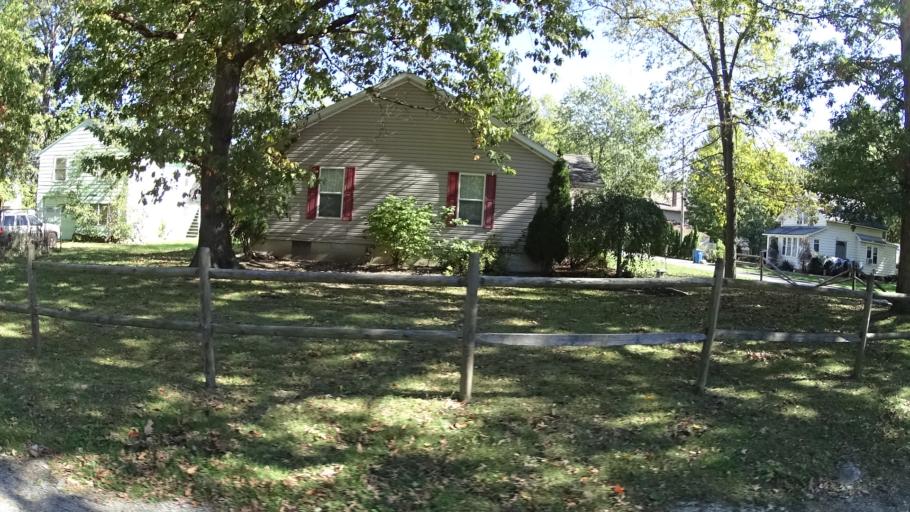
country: US
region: Ohio
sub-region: Lorain County
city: Lorain
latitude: 41.4341
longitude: -82.1670
